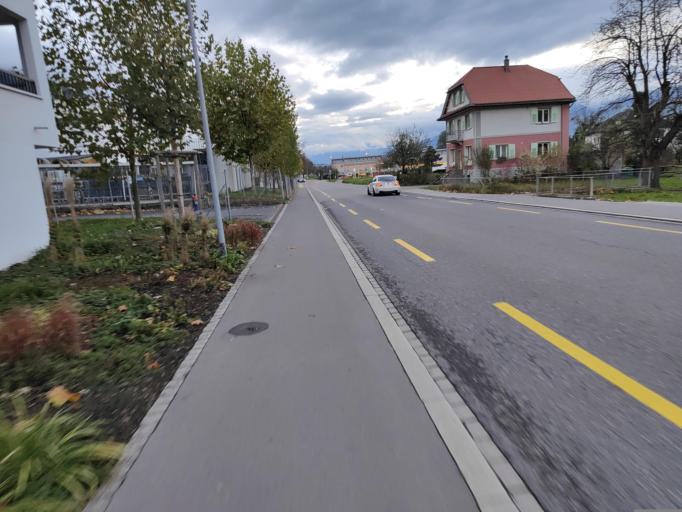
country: LI
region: Eschen
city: Eschen
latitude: 47.2096
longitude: 9.5275
